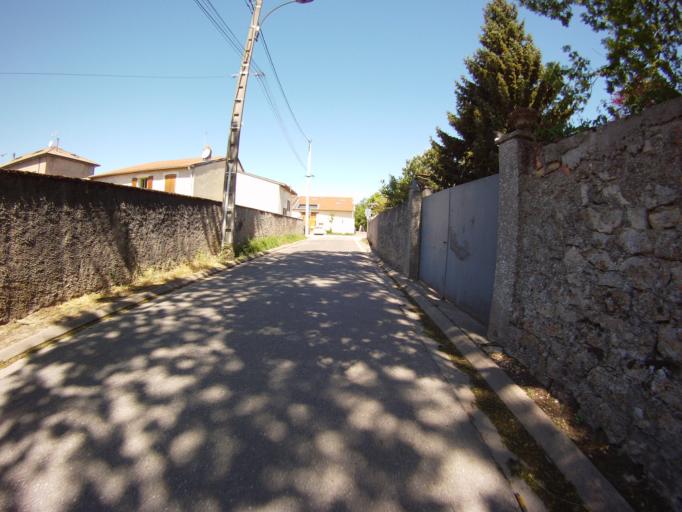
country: FR
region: Lorraine
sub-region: Departement de Meurthe-et-Moselle
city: Dommartin-les-Toul
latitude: 48.6505
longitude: 5.9057
